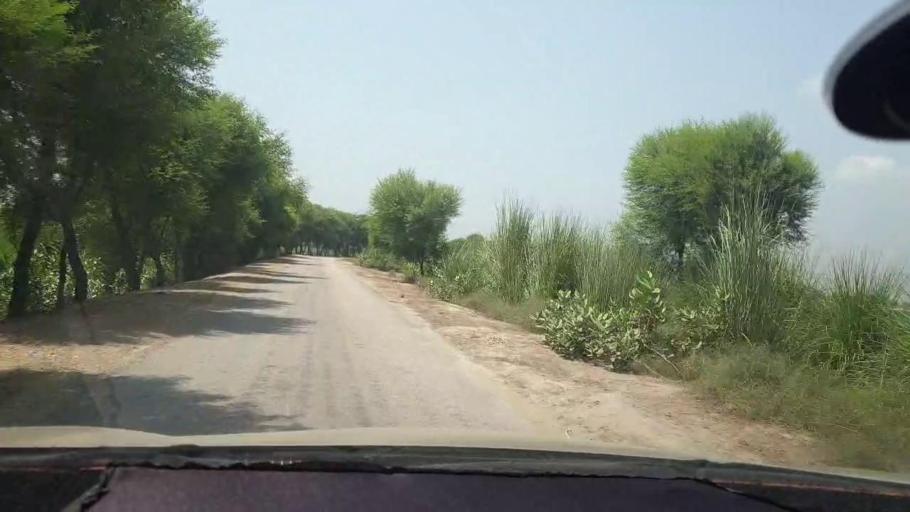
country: PK
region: Sindh
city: Kambar
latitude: 27.6637
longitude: 67.9210
